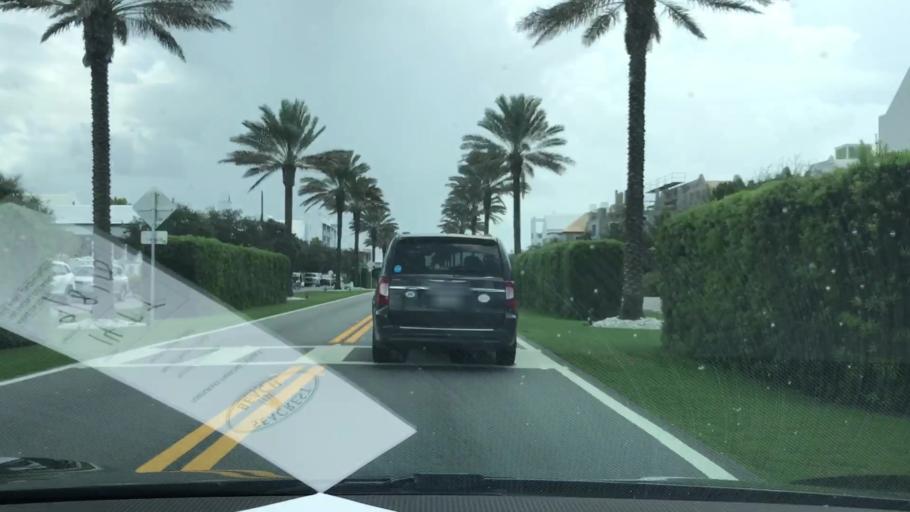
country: US
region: Florida
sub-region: Walton County
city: Seaside
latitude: 30.2856
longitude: -86.0312
